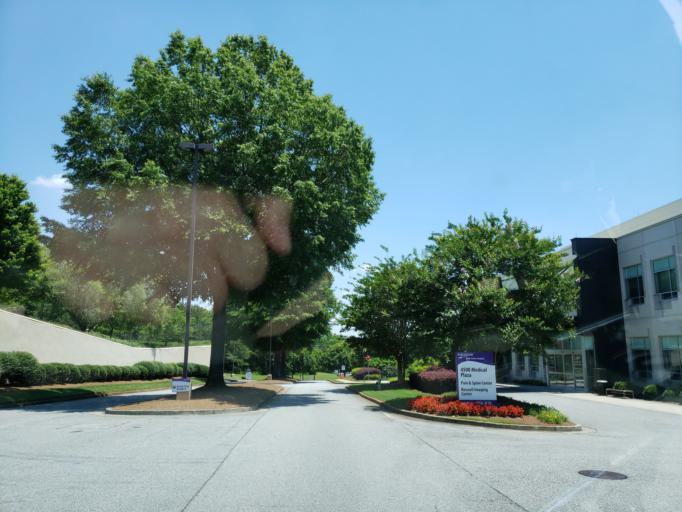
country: US
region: Georgia
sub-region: Fulton County
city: Alpharetta
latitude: 34.0623
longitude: -84.3206
